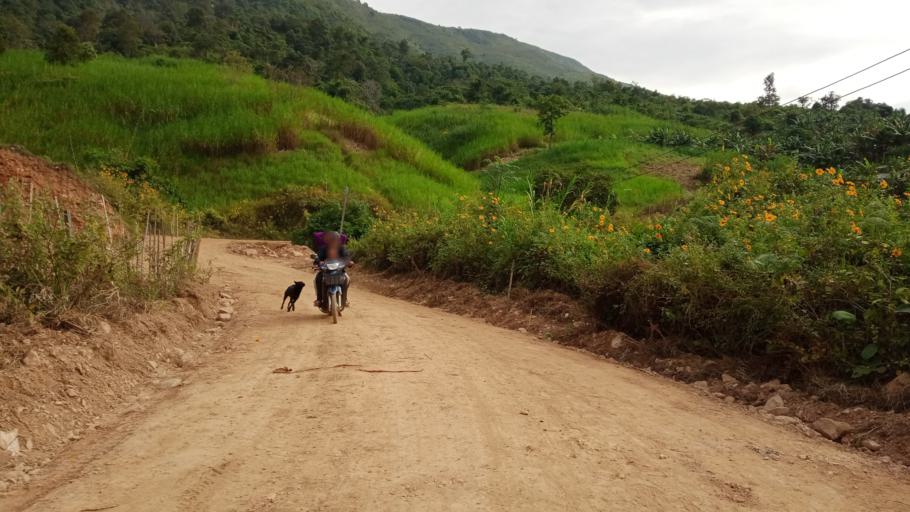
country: LA
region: Xiangkhoang
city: Phonsavan
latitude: 19.1186
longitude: 102.9142
